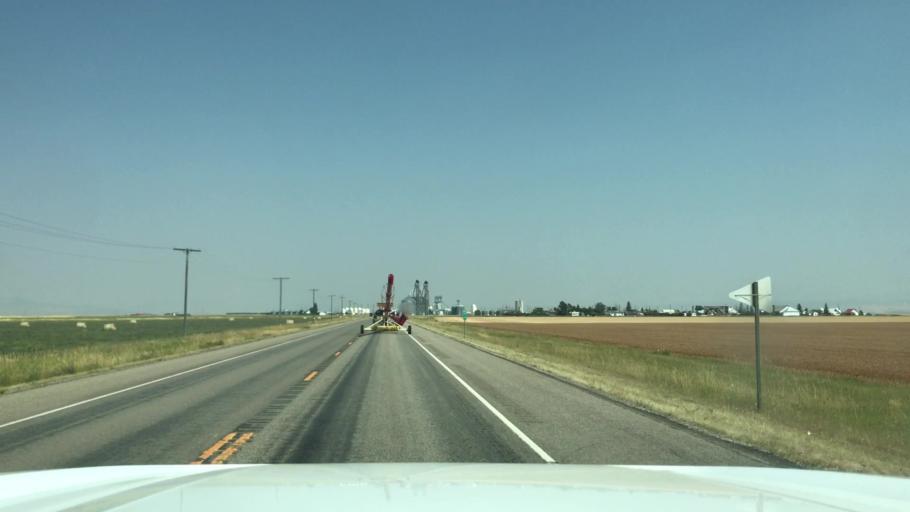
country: US
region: Montana
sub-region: Judith Basin County
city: Stanford
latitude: 47.0552
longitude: -109.9230
